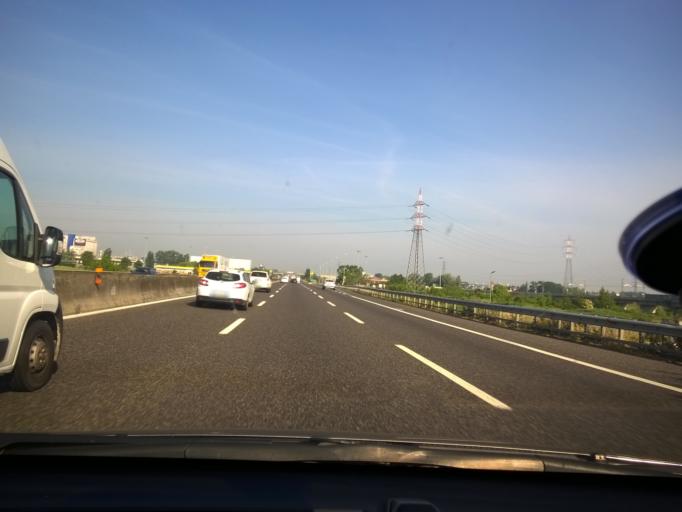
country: IT
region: Emilia-Romagna
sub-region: Provincia di Parma
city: San Prospero
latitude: 44.8253
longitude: 10.3830
